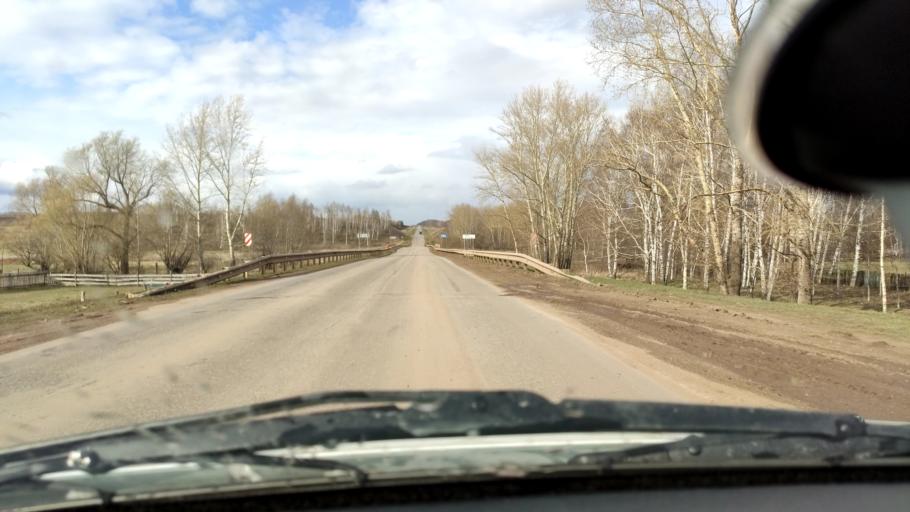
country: RU
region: Bashkortostan
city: Buzdyak
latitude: 54.6882
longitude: 54.5557
